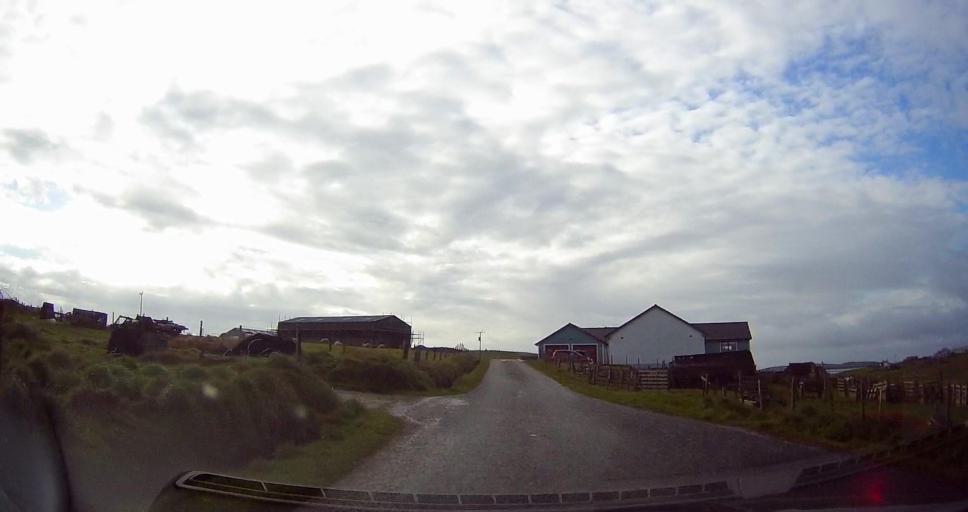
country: GB
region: Scotland
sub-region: Shetland Islands
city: Sandwick
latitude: 60.0438
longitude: -1.2053
